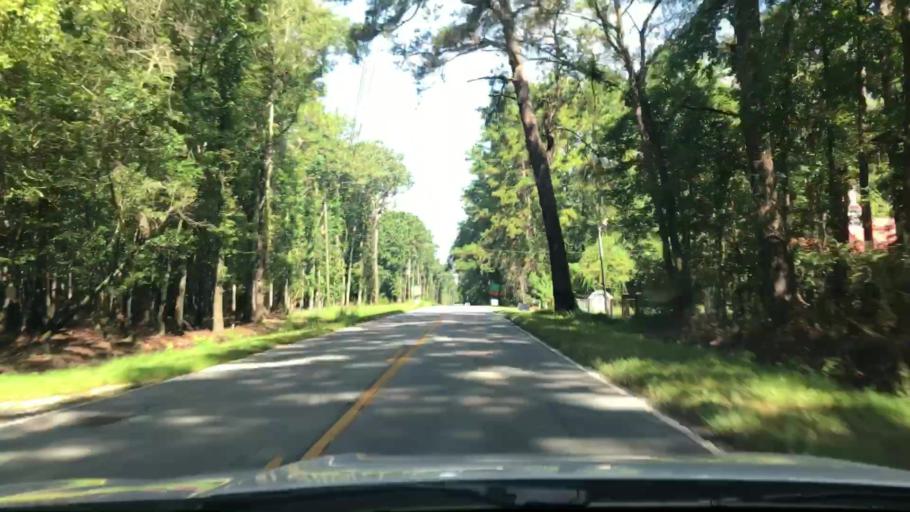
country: US
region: South Carolina
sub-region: Dorchester County
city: Centerville
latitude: 32.9332
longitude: -80.1758
